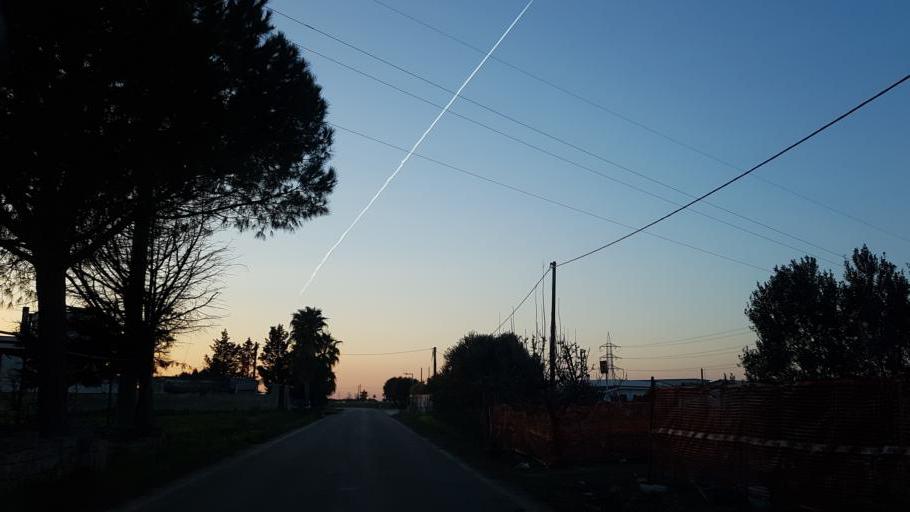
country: IT
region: Apulia
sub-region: Provincia di Brindisi
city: La Rosa
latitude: 40.5914
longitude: 17.9412
